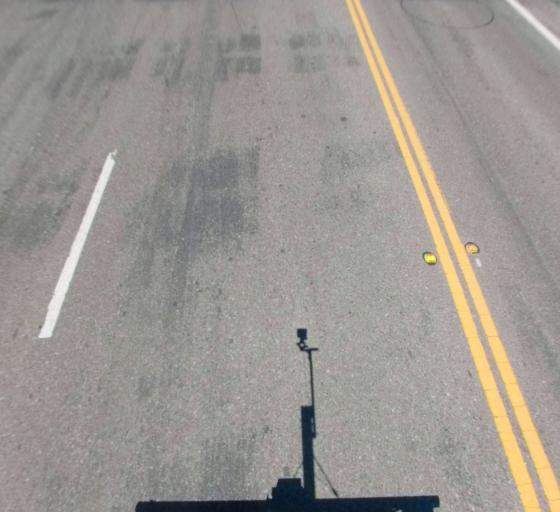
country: US
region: California
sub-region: Madera County
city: Parkwood
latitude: 36.9233
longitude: -120.0276
